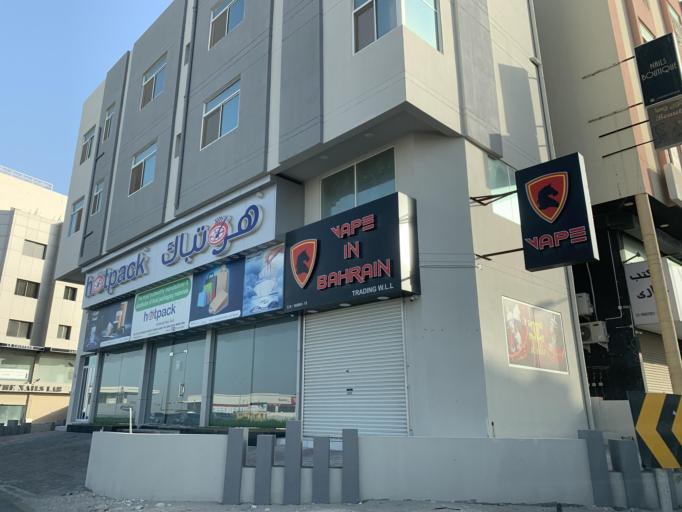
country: BH
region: Muharraq
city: Al Muharraq
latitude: 26.2808
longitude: 50.5981
